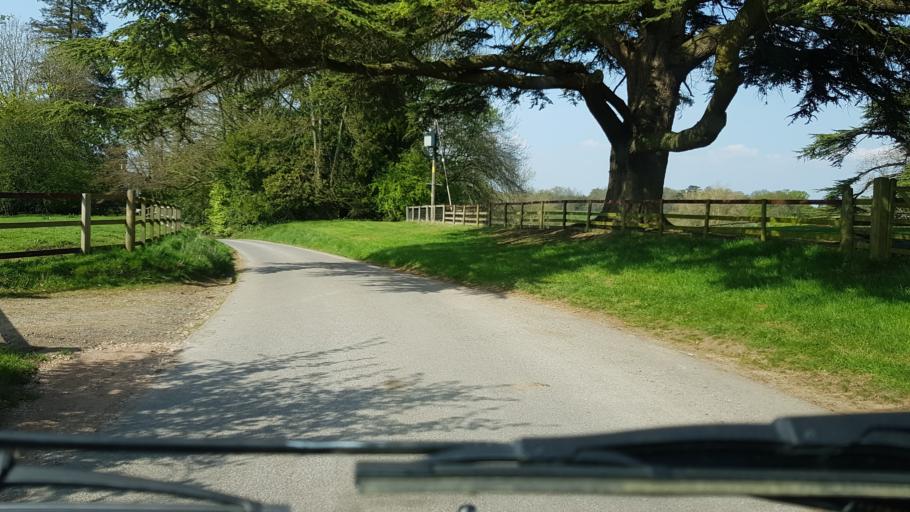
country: GB
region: England
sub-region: Hampshire
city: Highclere
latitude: 51.3293
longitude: -1.3610
